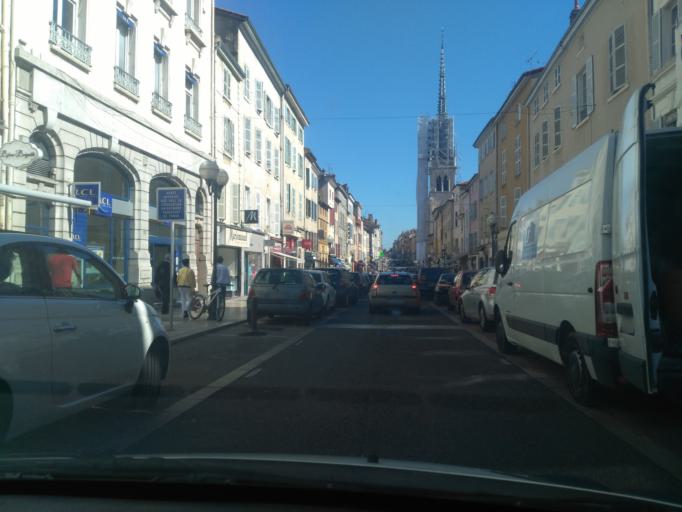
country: FR
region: Rhone-Alpes
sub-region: Departement du Rhone
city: Villefranche-sur-Saone
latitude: 45.9873
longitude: 4.7184
